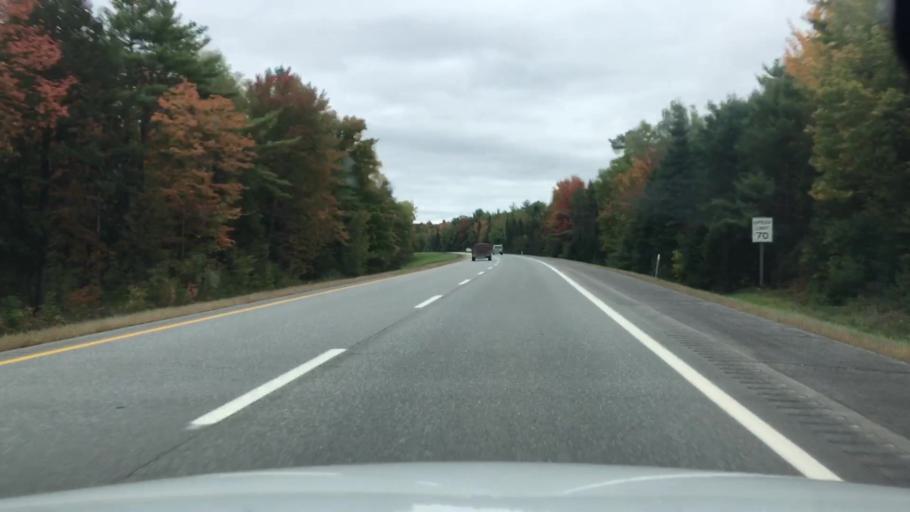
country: US
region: Maine
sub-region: Penobscot County
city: Plymouth
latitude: 44.7951
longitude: -69.2102
